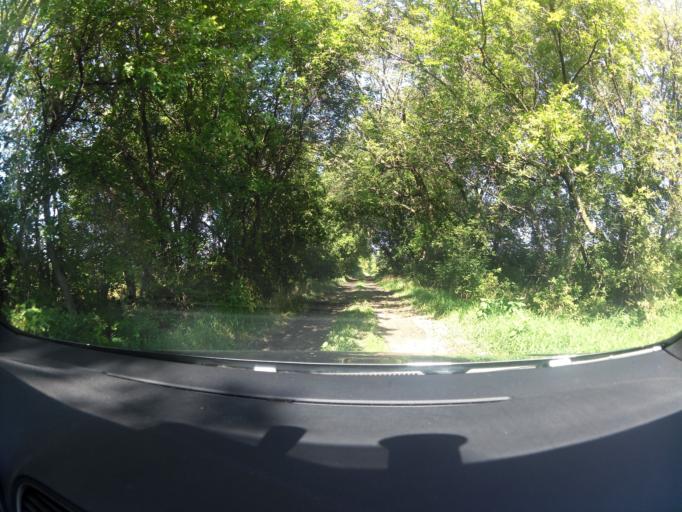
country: CA
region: Ontario
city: Arnprior
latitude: 45.3604
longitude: -76.2676
